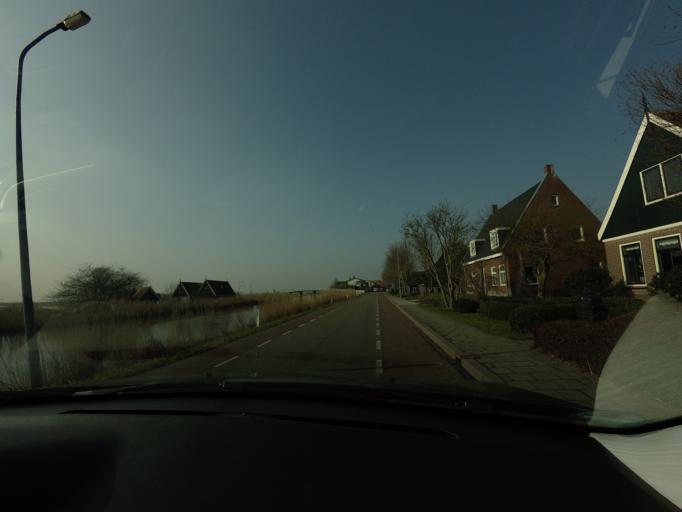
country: NL
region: North Holland
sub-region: Gemeente Heerhugowaard
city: Heerhugowaard
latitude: 52.6239
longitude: 4.8939
